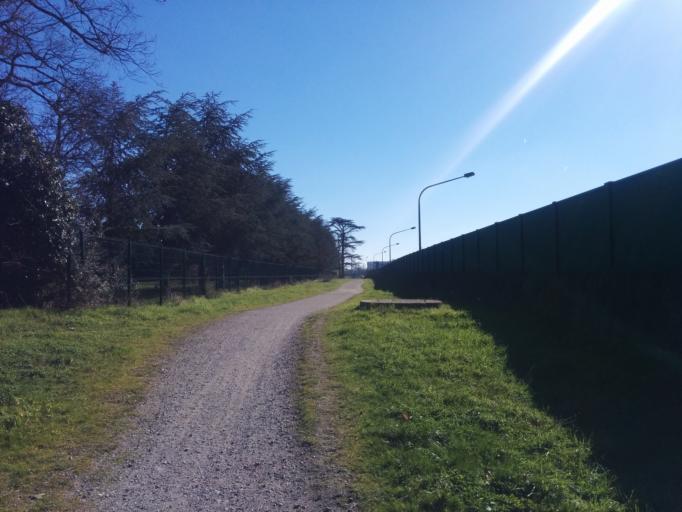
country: FR
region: Midi-Pyrenees
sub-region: Departement de la Haute-Garonne
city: Colomiers
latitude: 43.5826
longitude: 1.3642
